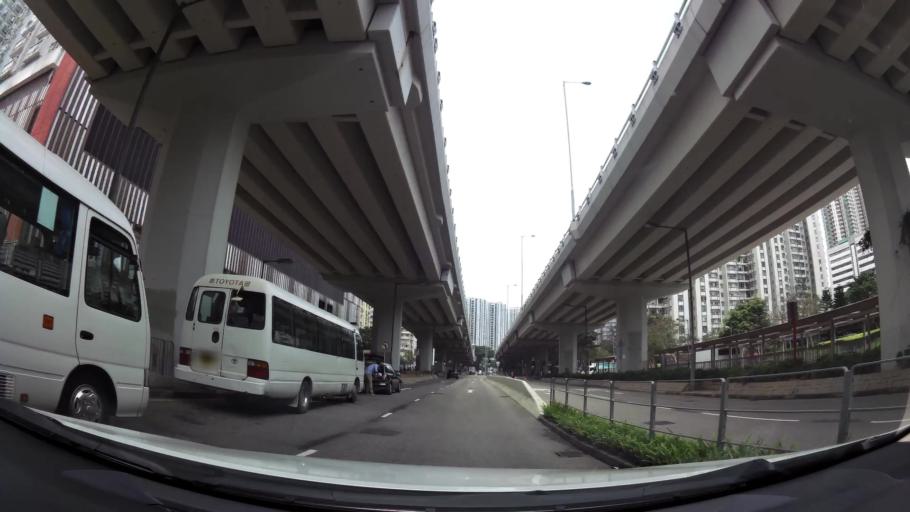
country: HK
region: Wanchai
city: Wan Chai
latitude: 22.2823
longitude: 114.2234
